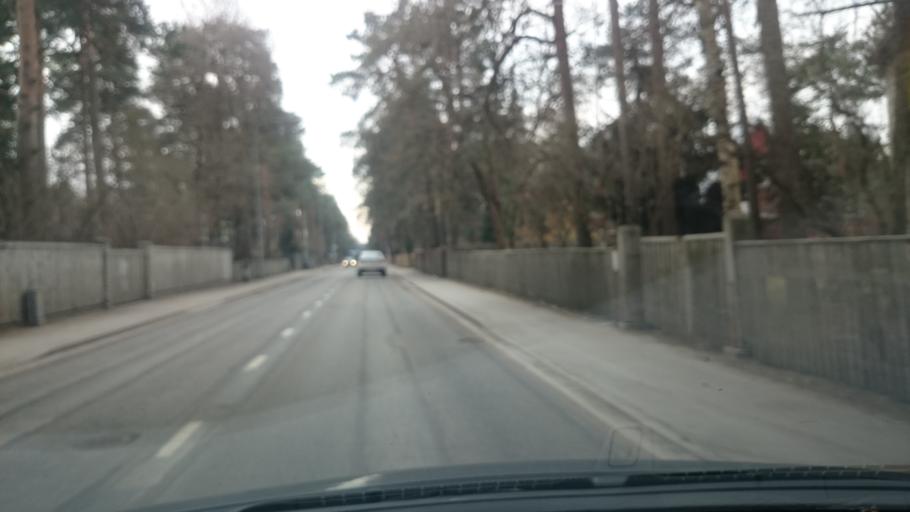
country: EE
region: Harju
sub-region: Saue vald
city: Laagri
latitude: 59.3711
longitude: 24.6322
